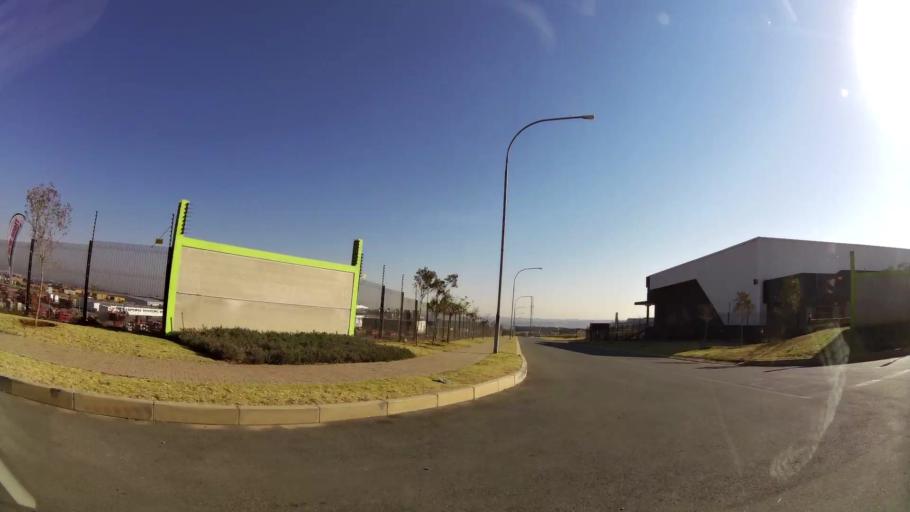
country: ZA
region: Gauteng
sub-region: City of Johannesburg Metropolitan Municipality
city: Modderfontein
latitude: -26.0543
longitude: 28.1688
